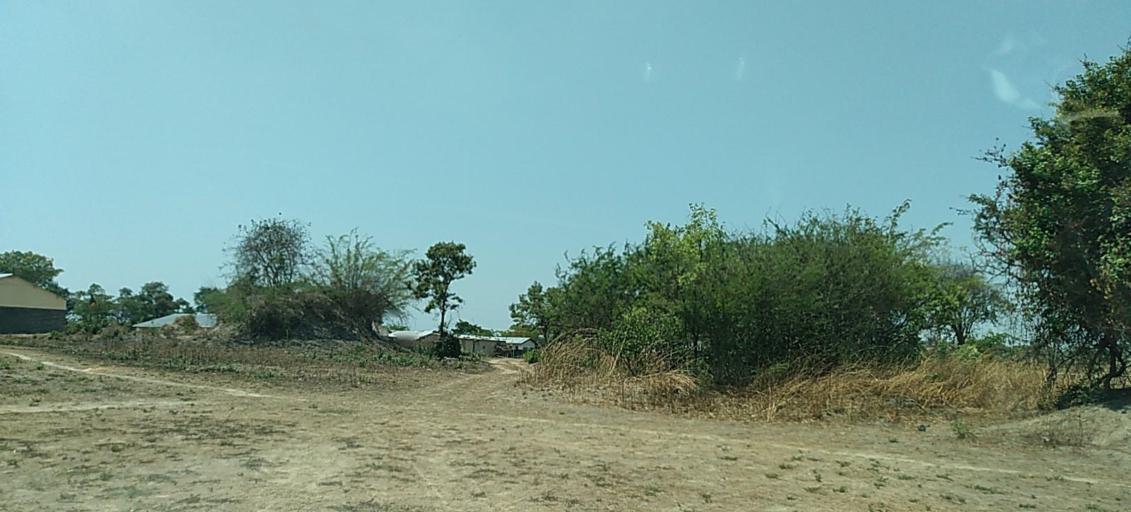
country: ZM
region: Copperbelt
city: Luanshya
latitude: -12.9930
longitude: 28.3261
